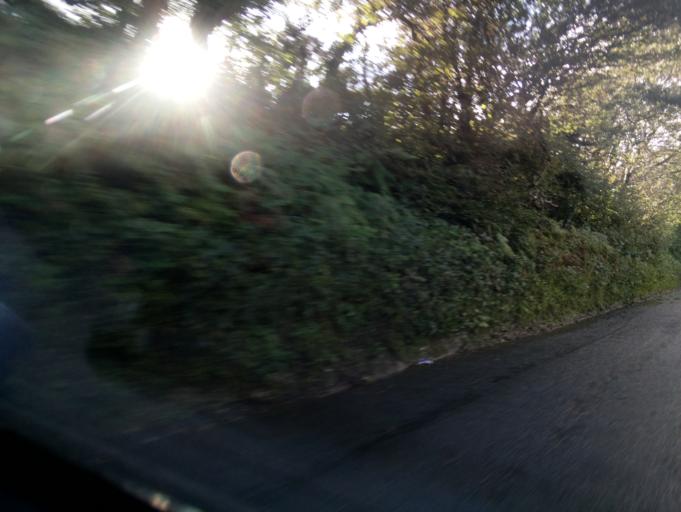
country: GB
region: England
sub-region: Devon
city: Totnes
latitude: 50.3590
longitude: -3.7311
